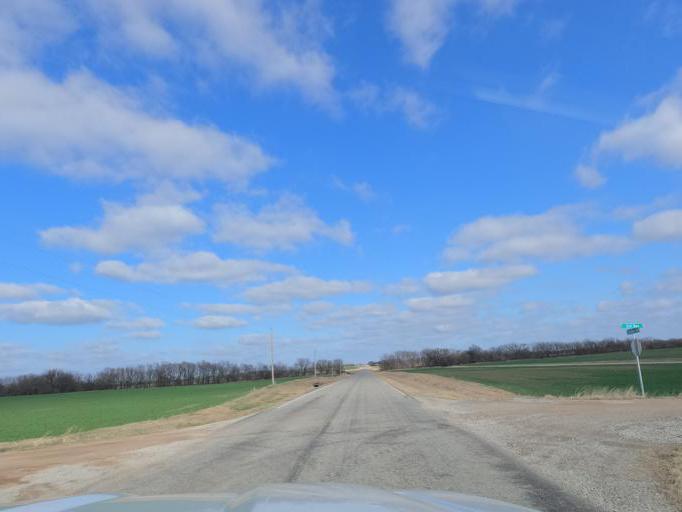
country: US
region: Kansas
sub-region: McPherson County
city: Inman
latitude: 38.2320
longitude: -97.8670
